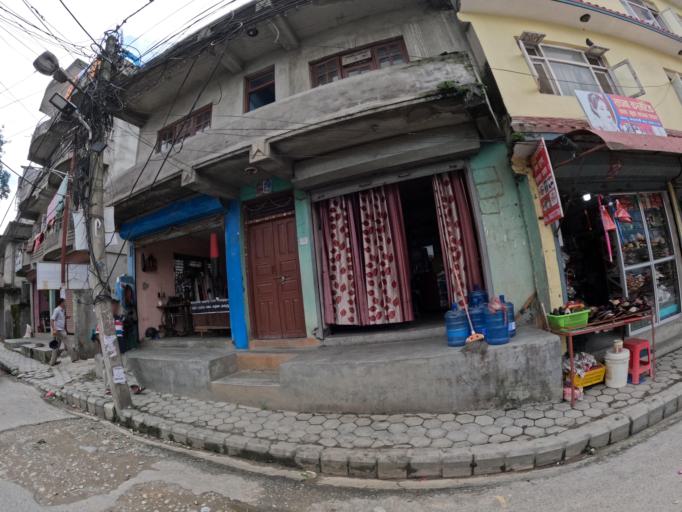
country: NP
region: Central Region
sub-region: Bagmati Zone
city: Kathmandu
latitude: 27.7391
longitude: 85.3166
